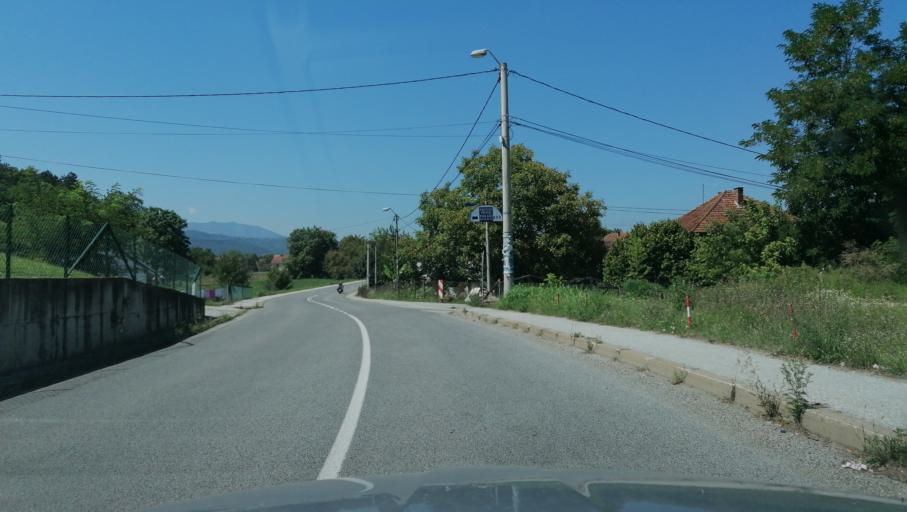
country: RS
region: Central Serbia
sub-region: Raski Okrug
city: Kraljevo
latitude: 43.6887
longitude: 20.6202
